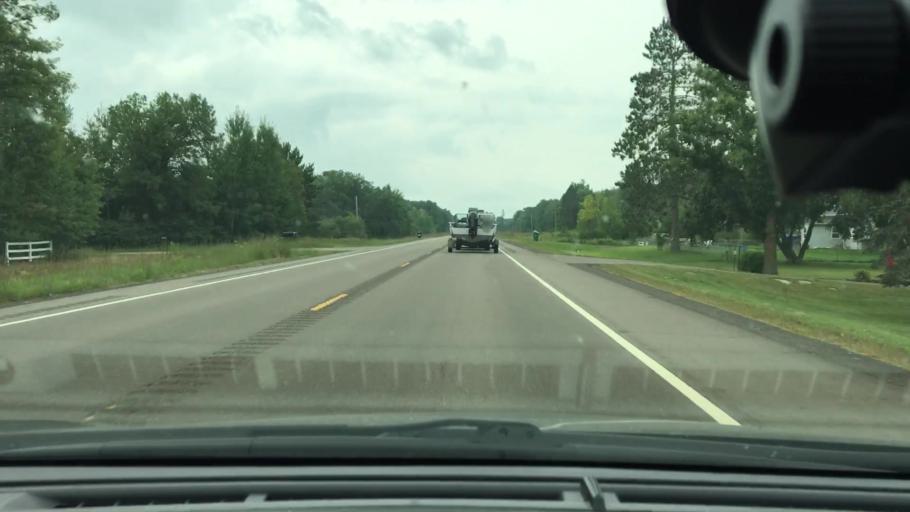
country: US
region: Minnesota
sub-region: Crow Wing County
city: Crosby
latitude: 46.5881
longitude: -93.9527
